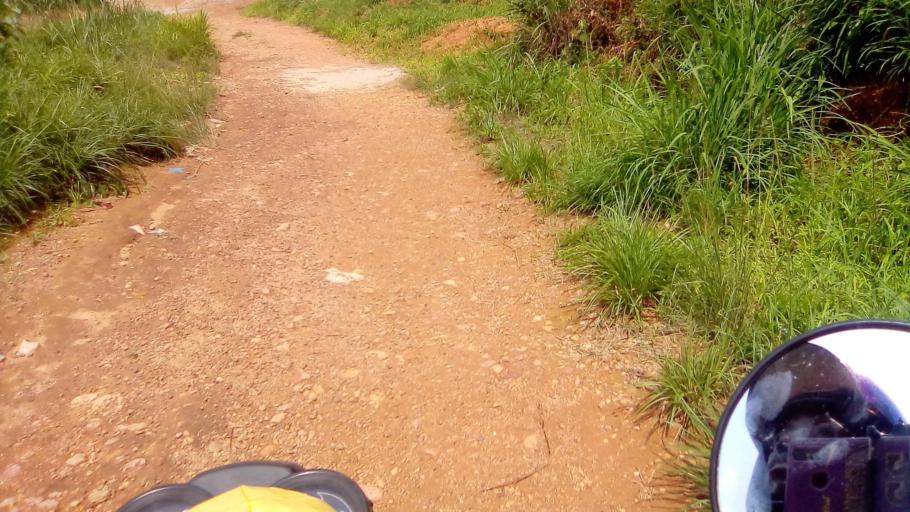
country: SL
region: Southern Province
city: Bo
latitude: 7.9755
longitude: -11.7441
